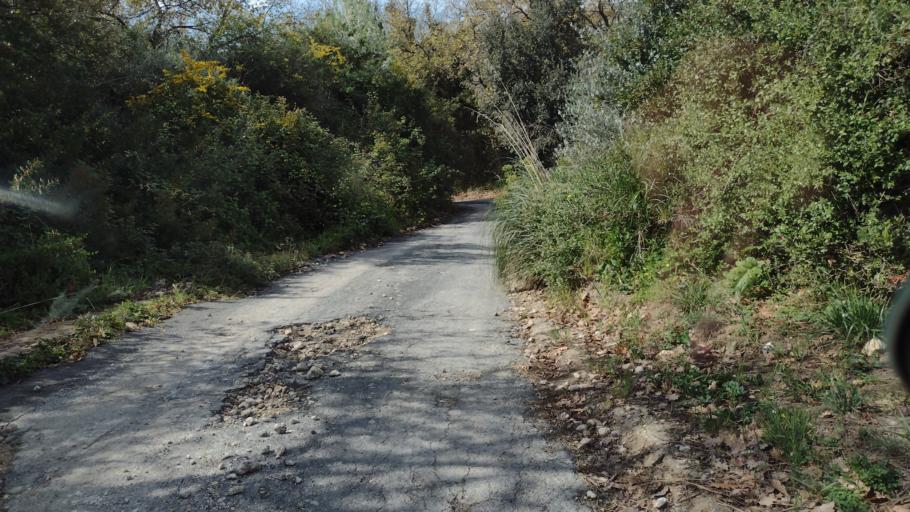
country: IT
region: Sicily
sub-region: Provincia di Siracusa
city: Noto
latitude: 36.9040
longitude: 15.0179
